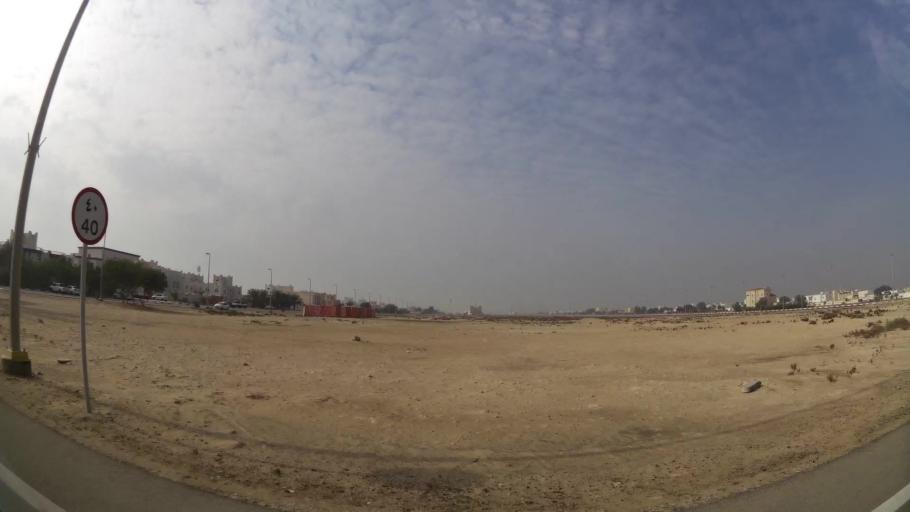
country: AE
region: Abu Dhabi
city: Abu Dhabi
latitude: 24.6660
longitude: 54.7701
